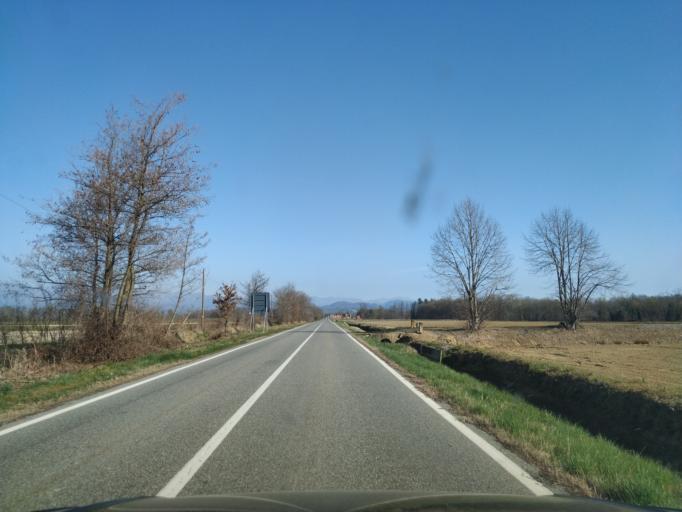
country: IT
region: Piedmont
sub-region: Provincia di Vercelli
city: Rovasenda
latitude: 45.5391
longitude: 8.3028
